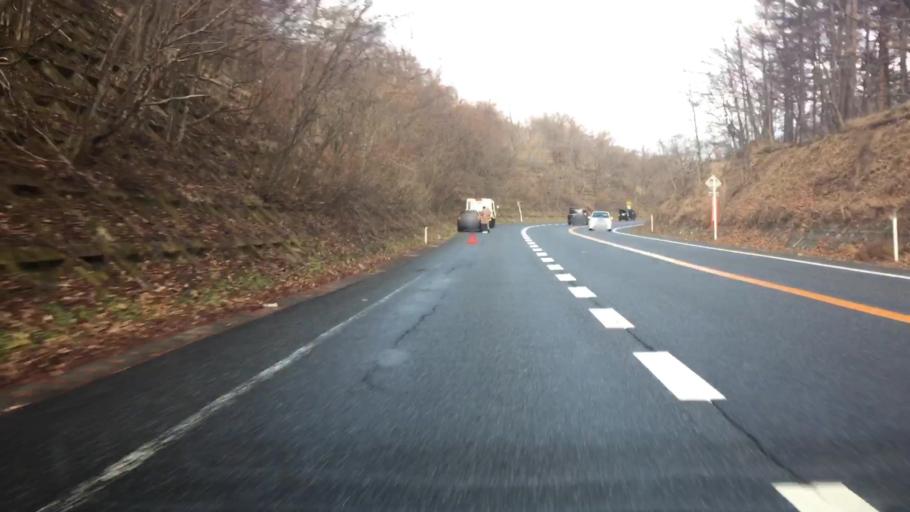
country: JP
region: Nagano
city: Saku
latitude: 36.3017
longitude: 138.6636
